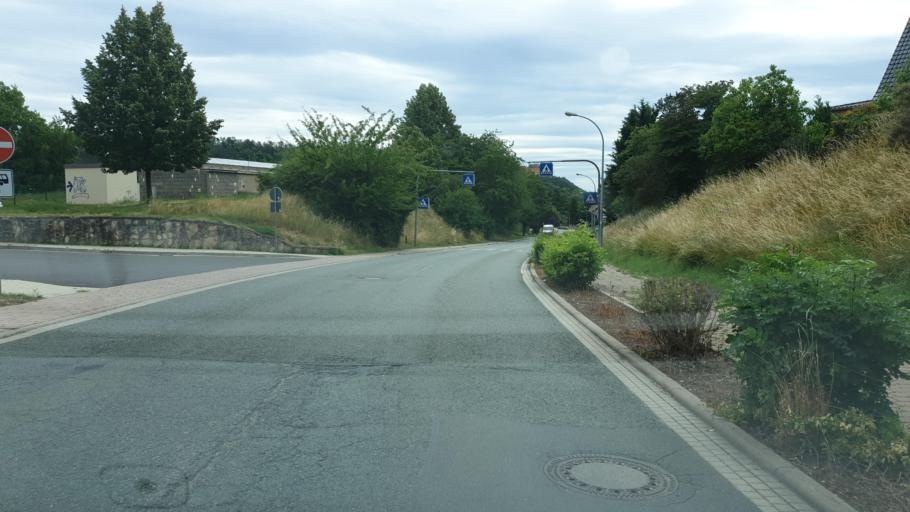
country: DE
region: Saxony-Anhalt
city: Freyburg
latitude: 51.2205
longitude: 11.7665
